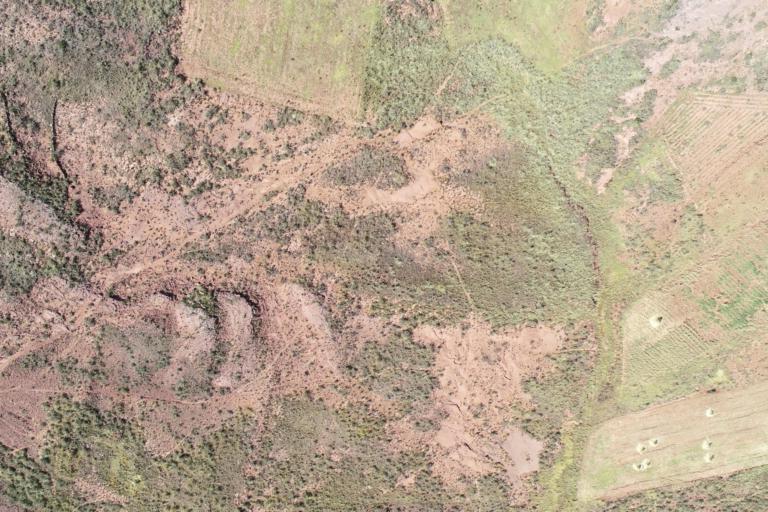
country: BO
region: La Paz
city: Tiahuanaco
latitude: -16.5992
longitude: -68.7582
